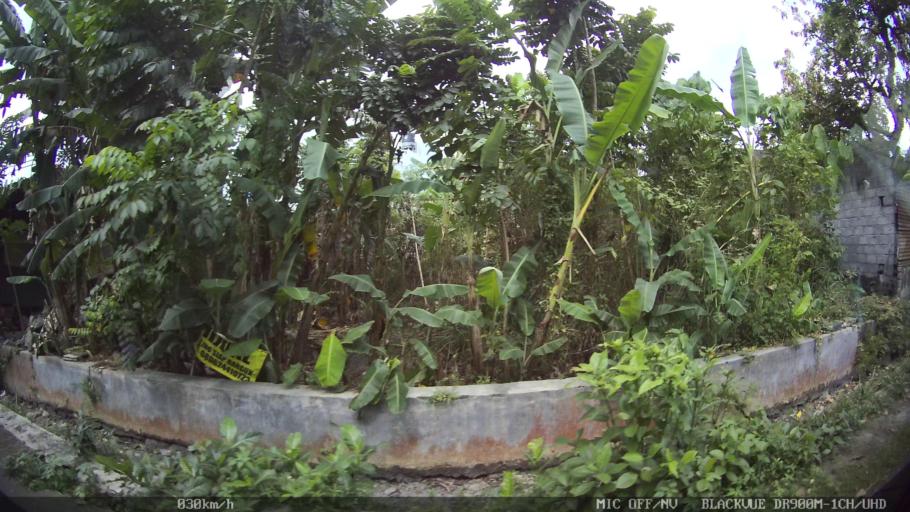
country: ID
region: Daerah Istimewa Yogyakarta
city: Yogyakarta
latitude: -7.7656
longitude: 110.3564
